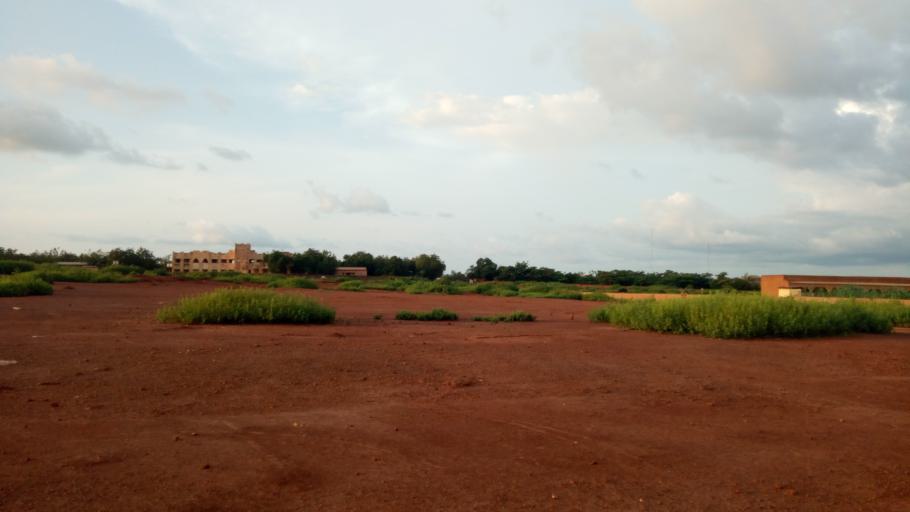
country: ML
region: Sikasso
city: Koutiala
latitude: 12.3749
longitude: -5.4786
